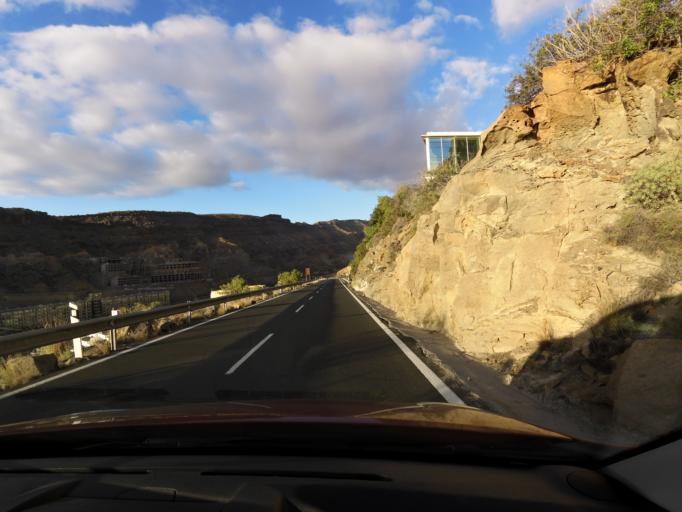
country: ES
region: Canary Islands
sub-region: Provincia de Las Palmas
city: Puerto Rico
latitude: 27.8136
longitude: -15.7514
